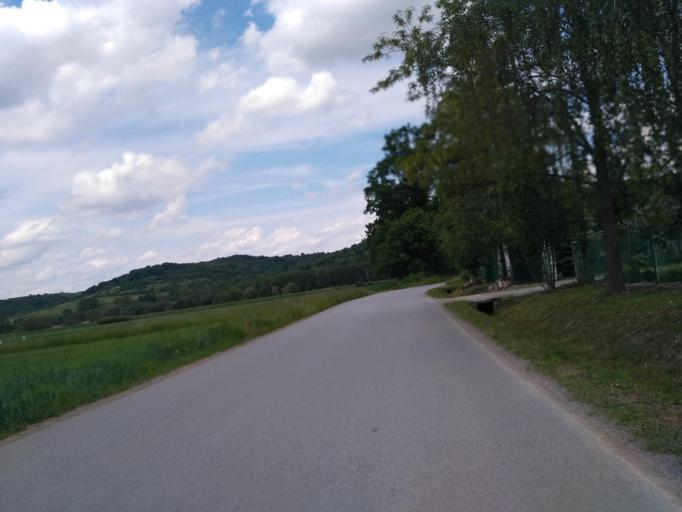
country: PL
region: Subcarpathian Voivodeship
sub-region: Powiat krosnienski
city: Chorkowka
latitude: 49.6051
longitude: 21.6220
